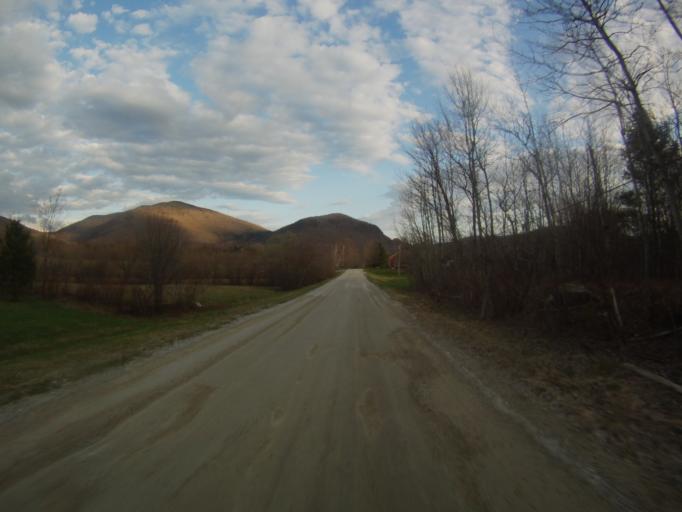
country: US
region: Vermont
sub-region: Rutland County
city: Brandon
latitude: 43.8506
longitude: -72.9978
